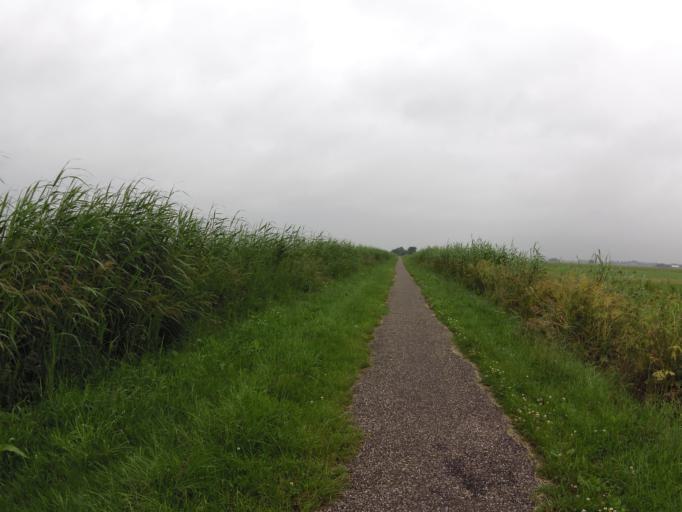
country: NL
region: Utrecht
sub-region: Gemeente Woerden
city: Woerden
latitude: 52.1288
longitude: 4.9428
